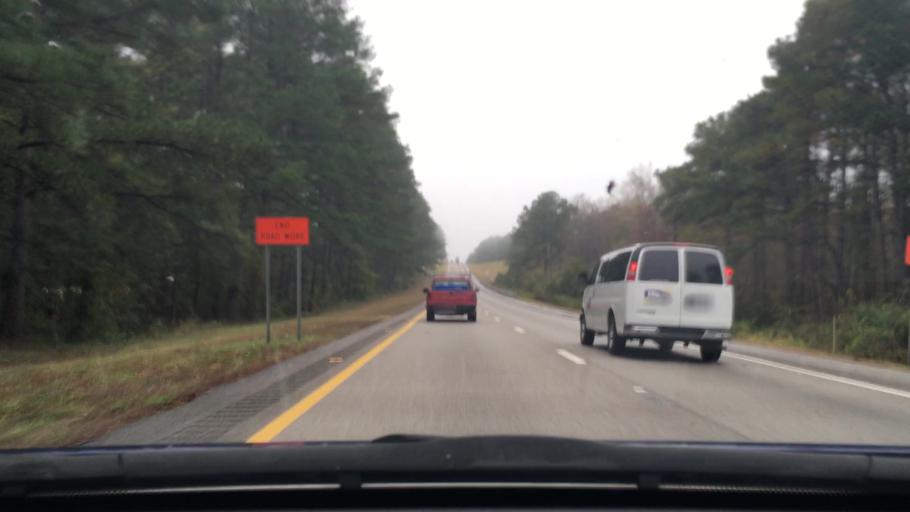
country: US
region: South Carolina
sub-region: Kershaw County
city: Camden
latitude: 34.2085
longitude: -80.4565
